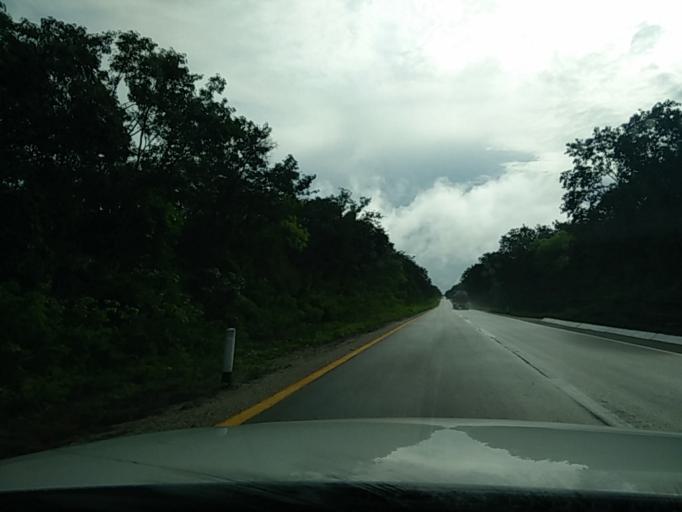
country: MX
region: Yucatan
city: Tunkas
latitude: 20.7600
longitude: -88.7739
